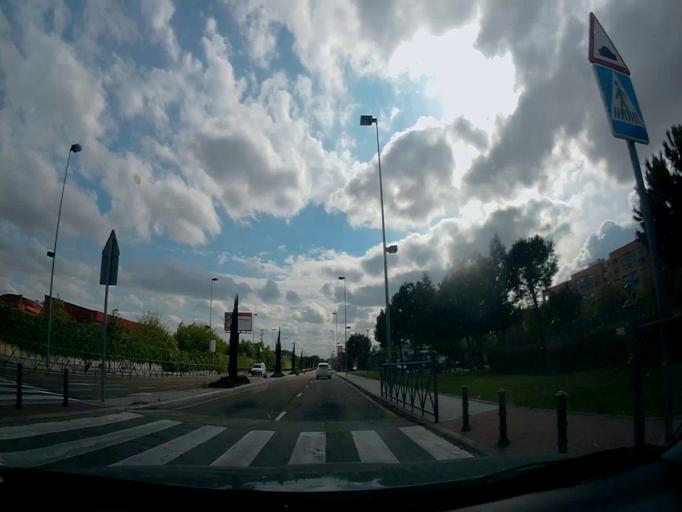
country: ES
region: Madrid
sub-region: Provincia de Madrid
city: Alcorcon
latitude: 40.3441
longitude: -3.8390
